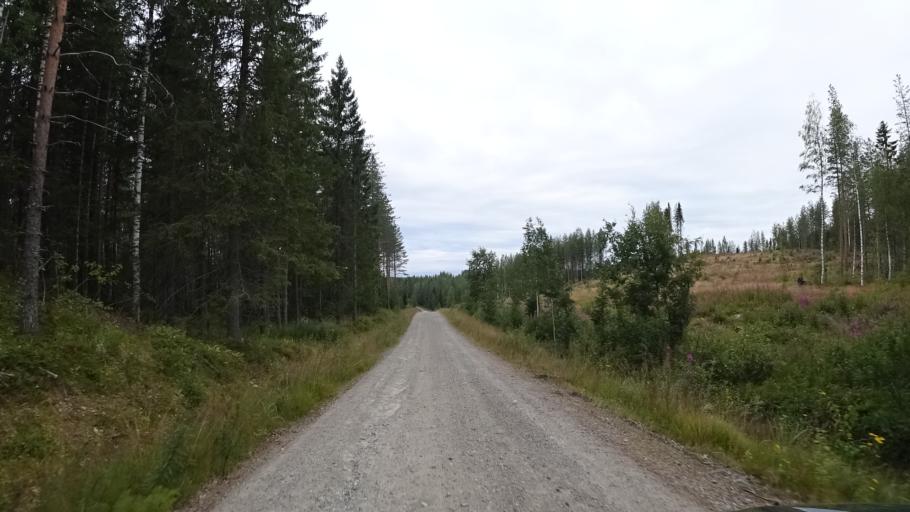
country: FI
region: North Karelia
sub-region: Joensuu
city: Ilomantsi
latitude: 63.1519
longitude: 30.6459
